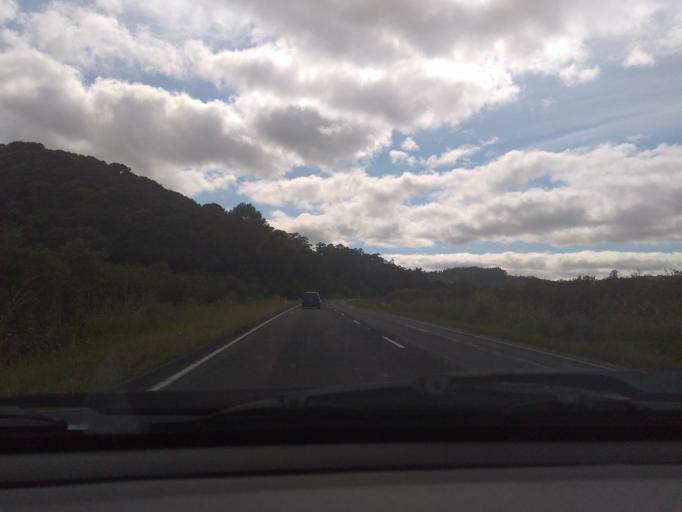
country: NZ
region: Northland
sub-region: Far North District
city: Taipa
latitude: -35.0115
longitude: 173.5461
